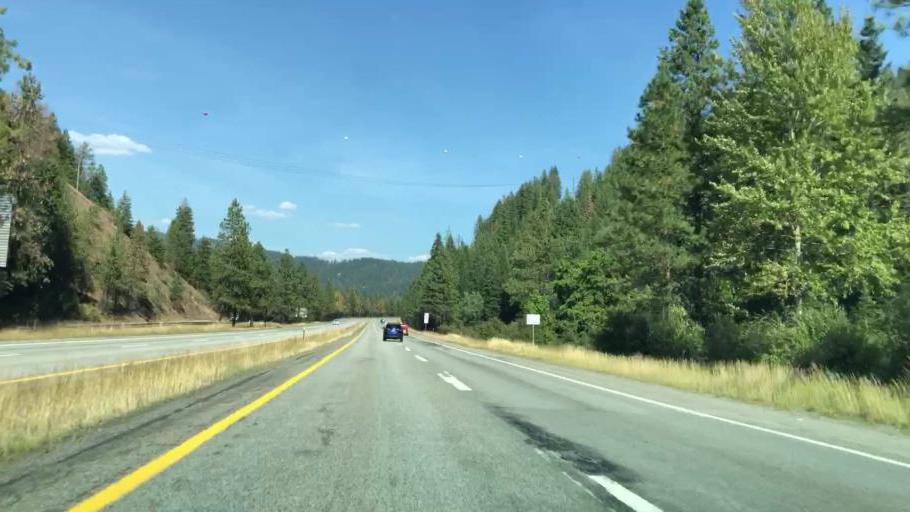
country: US
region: Idaho
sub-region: Shoshone County
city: Pinehurst
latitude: 47.5759
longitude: -116.4376
